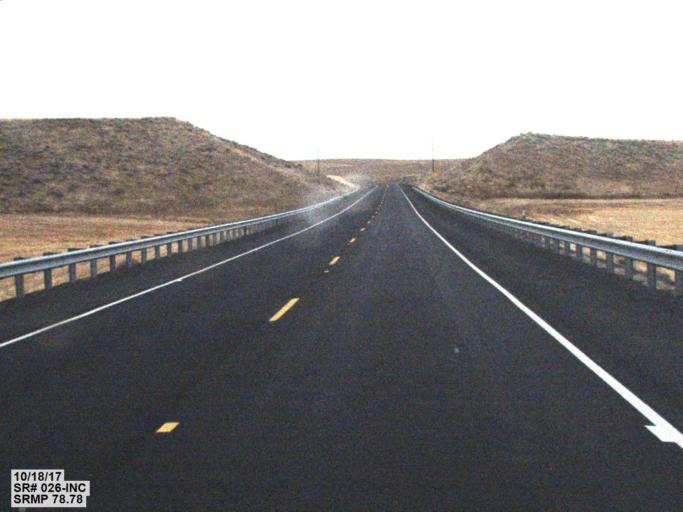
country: US
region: Washington
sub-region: Adams County
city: Ritzville
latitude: 46.7843
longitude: -118.3836
